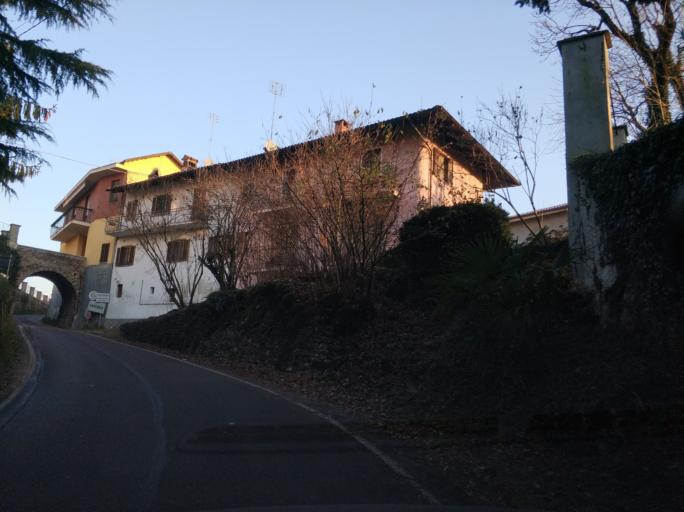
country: IT
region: Piedmont
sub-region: Provincia di Torino
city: Barbania
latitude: 45.2903
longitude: 7.6311
